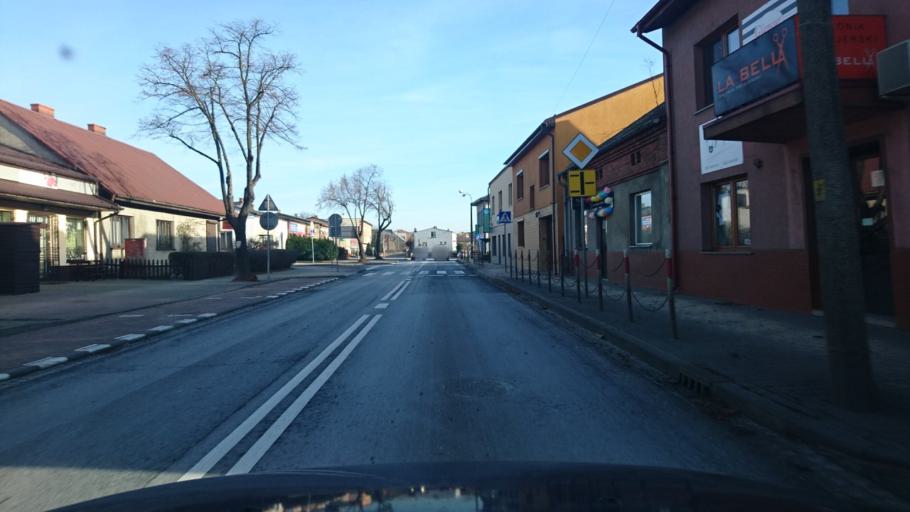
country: PL
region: Opole Voivodeship
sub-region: Powiat oleski
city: Dalachow
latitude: 51.0381
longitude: 18.6002
